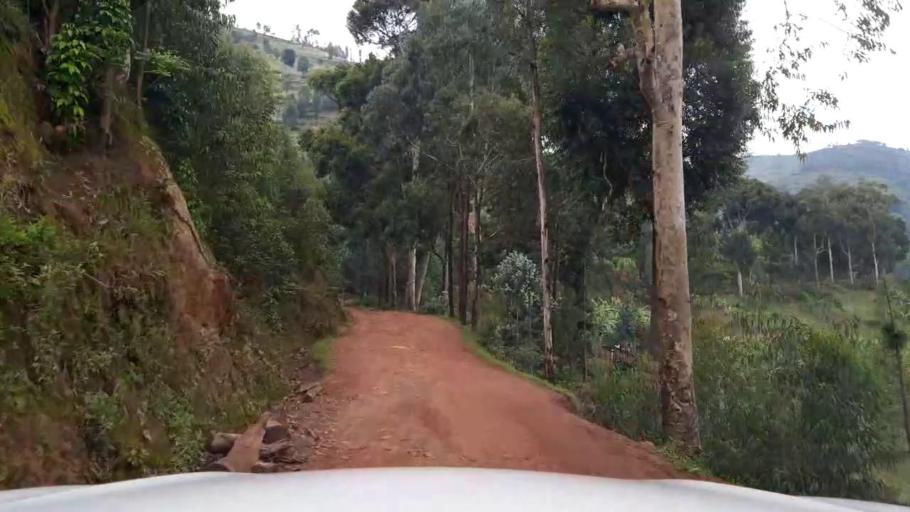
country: UG
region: Western Region
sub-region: Kisoro District
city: Kisoro
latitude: -1.3925
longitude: 29.7981
